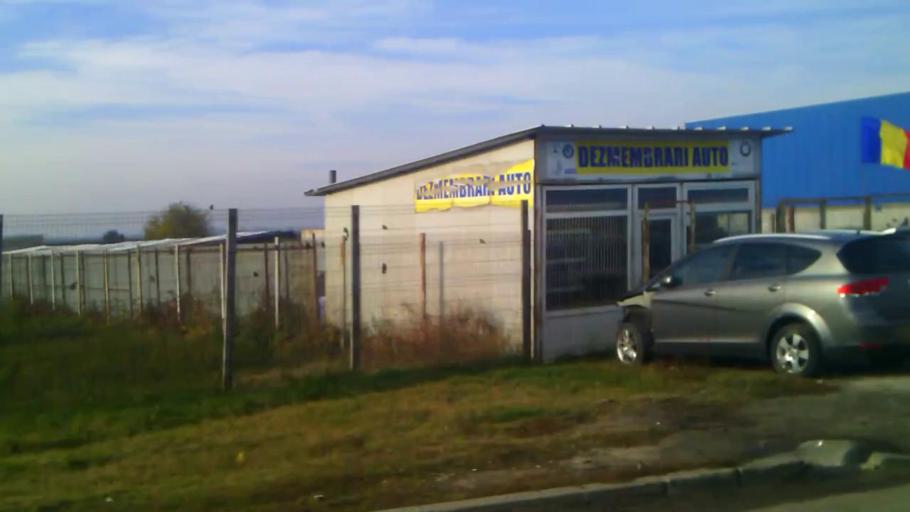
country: RO
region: Ilfov
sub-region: Comuna Popesti-Leordeni
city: Popesti-Leordeni
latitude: 44.3464
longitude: 26.1603
